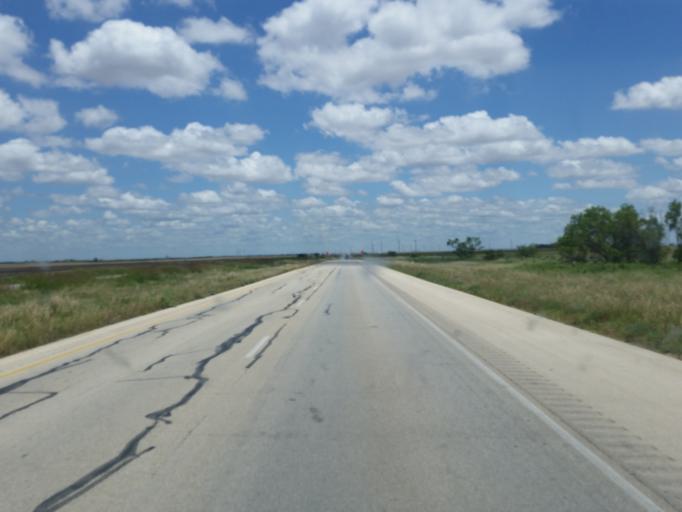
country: US
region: Texas
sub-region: Nolan County
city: Roscoe
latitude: 32.4862
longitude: -100.6268
